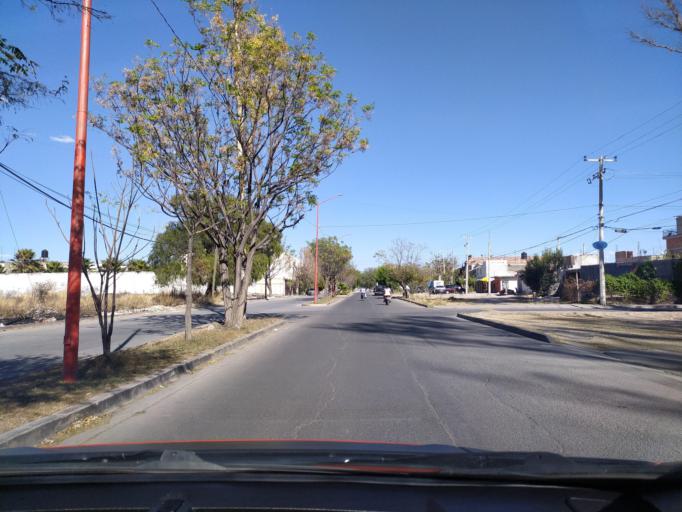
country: MX
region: Guanajuato
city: San Francisco del Rincon
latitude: 21.0199
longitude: -101.8479
